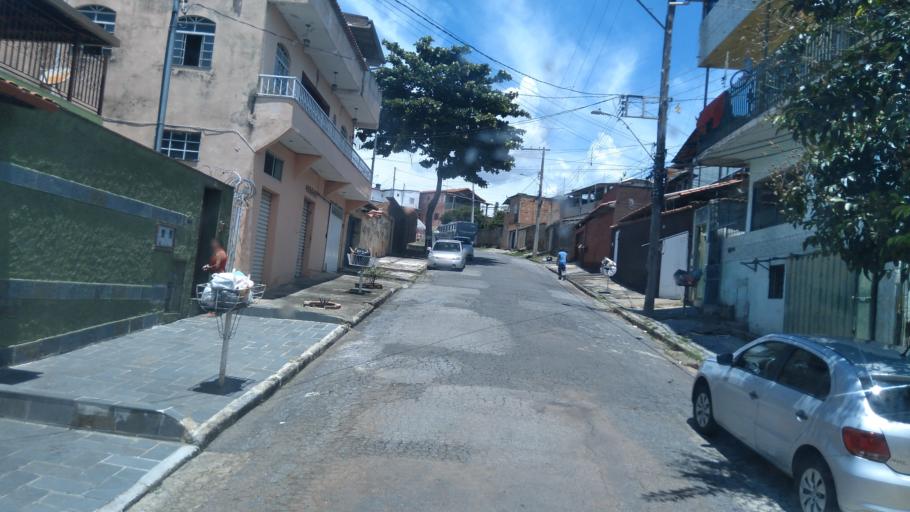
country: BR
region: Minas Gerais
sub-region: Belo Horizonte
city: Belo Horizonte
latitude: -19.8615
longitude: -43.8967
